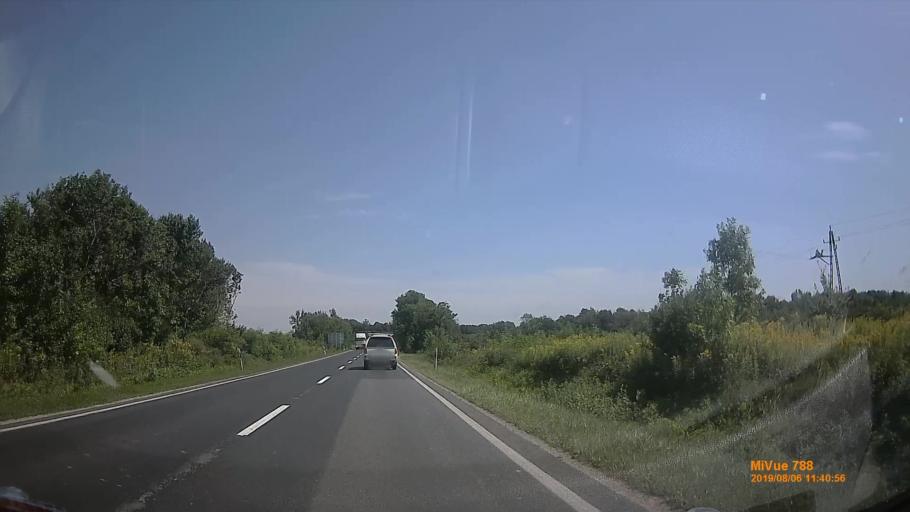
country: HU
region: Vas
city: Kormend
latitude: 46.9854
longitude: 16.5240
